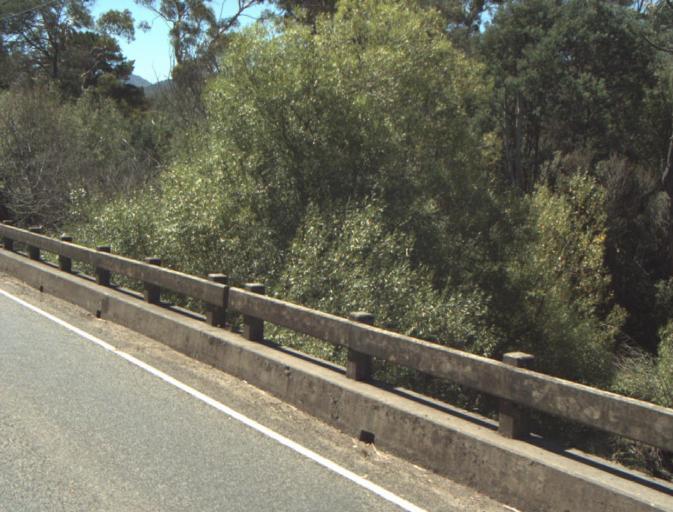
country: AU
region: Tasmania
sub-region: Launceston
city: Newstead
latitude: -41.3895
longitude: 147.3005
